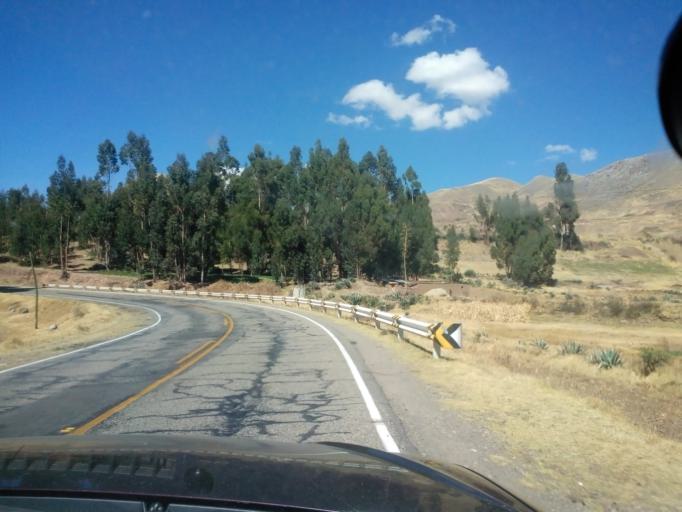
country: PE
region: Cusco
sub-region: Provincia de Canchis
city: Combapata
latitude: -14.0985
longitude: -71.4371
